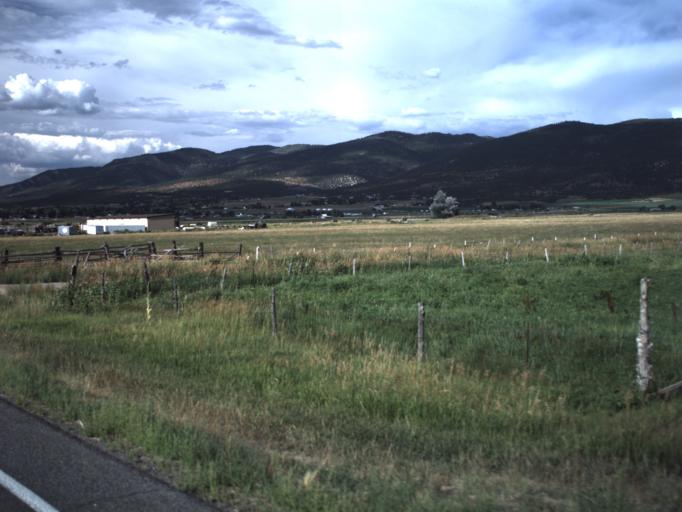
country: US
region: Utah
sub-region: Sanpete County
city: Fairview
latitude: 39.6046
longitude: -111.4447
